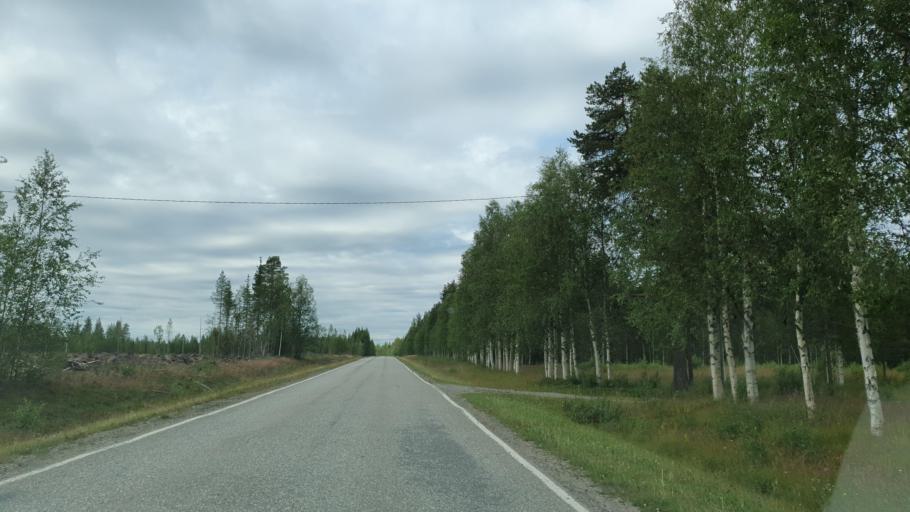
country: FI
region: Lapland
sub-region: Tunturi-Lappi
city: Kittilae
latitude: 67.6157
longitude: 25.3499
